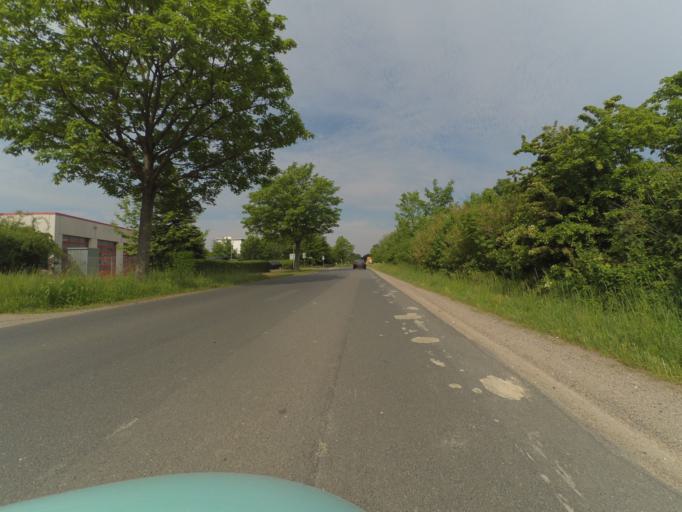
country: DE
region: Lower Saxony
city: Lehrte
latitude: 52.3679
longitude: 9.9940
